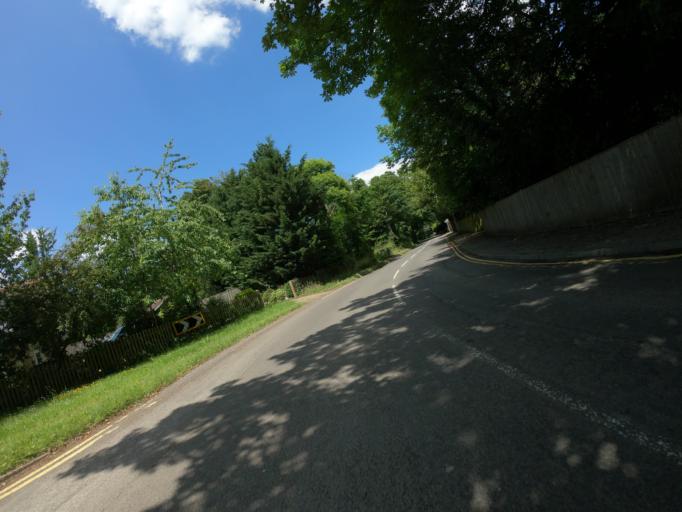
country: GB
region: England
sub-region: Kent
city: Halstead
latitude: 51.2793
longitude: 0.1269
